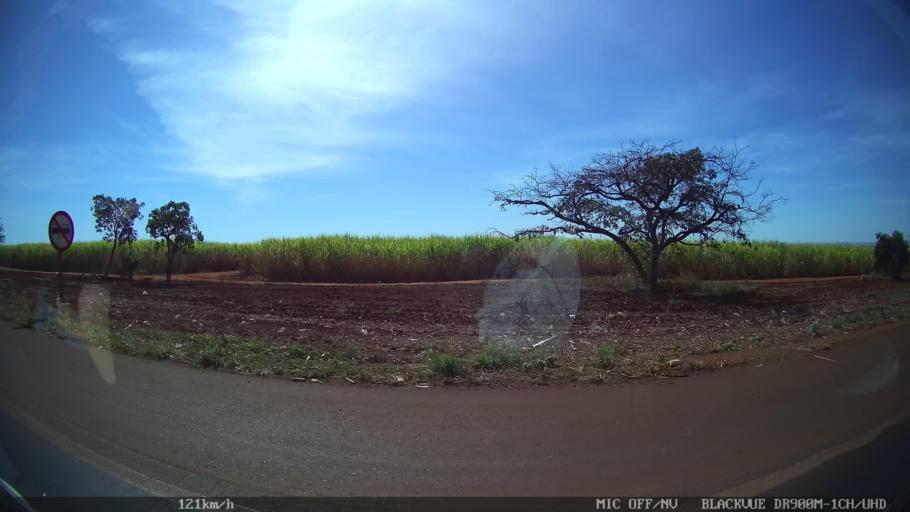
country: BR
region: Sao Paulo
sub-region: Ipua
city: Ipua
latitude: -20.4986
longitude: -47.9609
